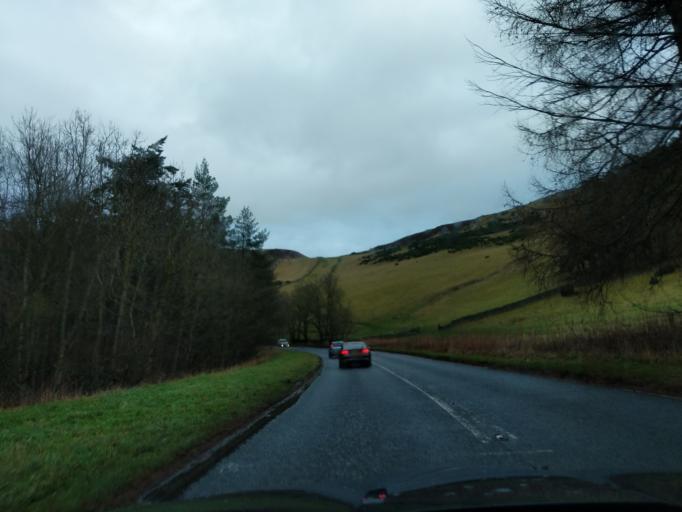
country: GB
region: Scotland
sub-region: The Scottish Borders
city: Galashiels
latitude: 55.6598
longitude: -2.8615
